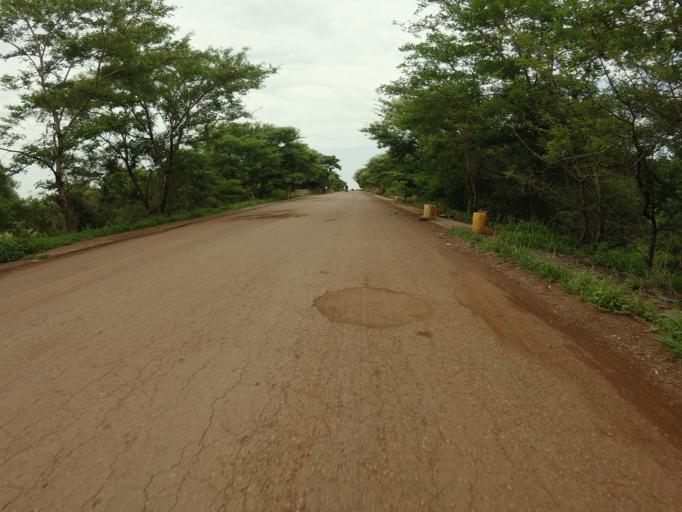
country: GH
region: Upper East
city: Bawku
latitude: 11.0027
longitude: -0.3872
